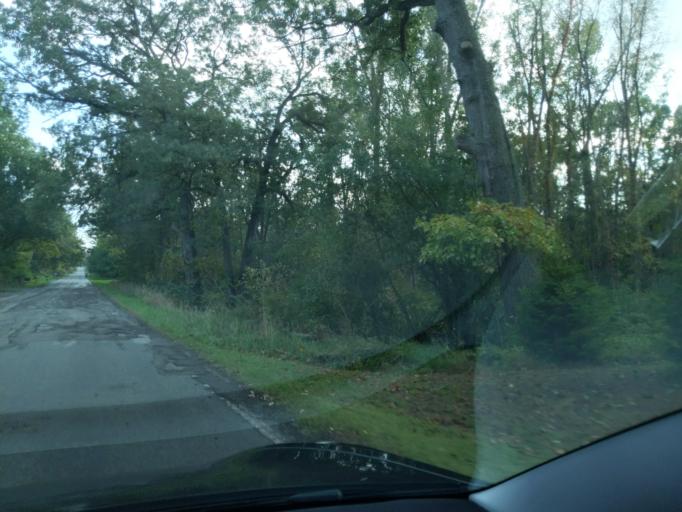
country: US
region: Michigan
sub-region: Jackson County
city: Jackson
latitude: 42.2881
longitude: -84.4831
